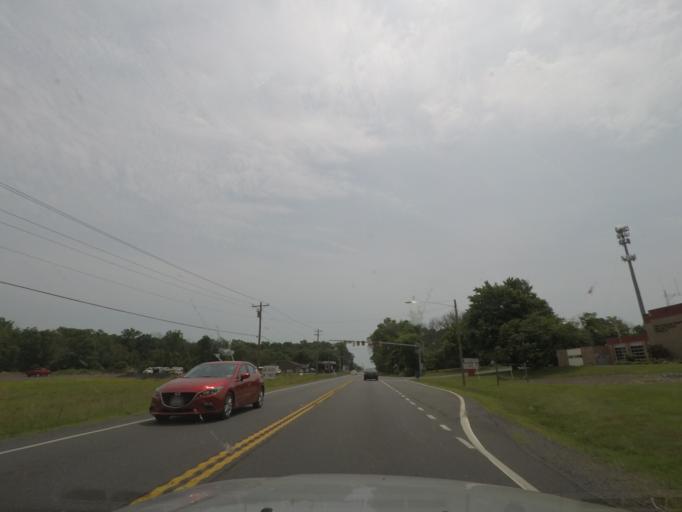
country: US
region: Virginia
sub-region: Prince William County
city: Bull Run Mountain Estates
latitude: 38.8814
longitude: -77.6336
